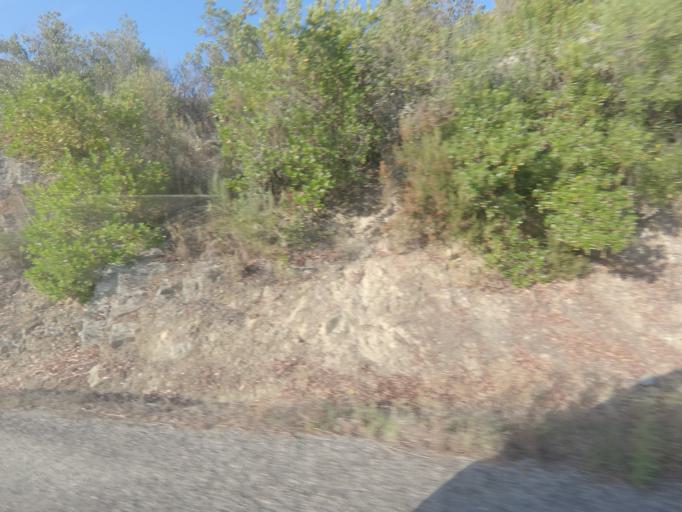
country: PT
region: Viseu
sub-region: Armamar
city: Armamar
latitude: 41.1297
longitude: -7.6738
